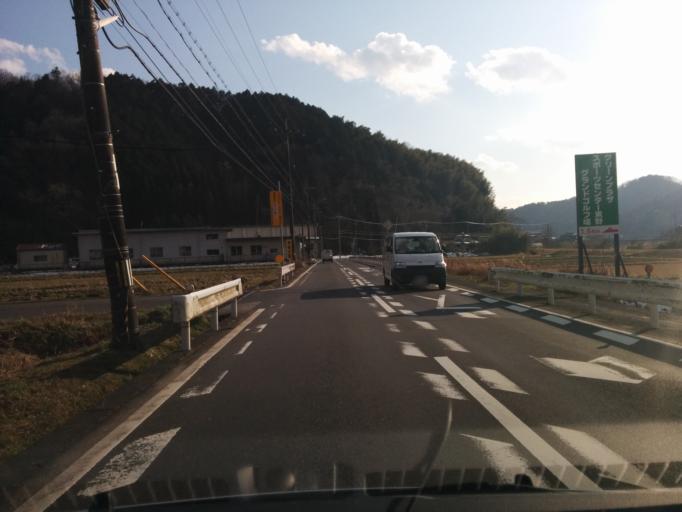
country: JP
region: Kyoto
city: Ayabe
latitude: 35.3455
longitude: 135.2195
